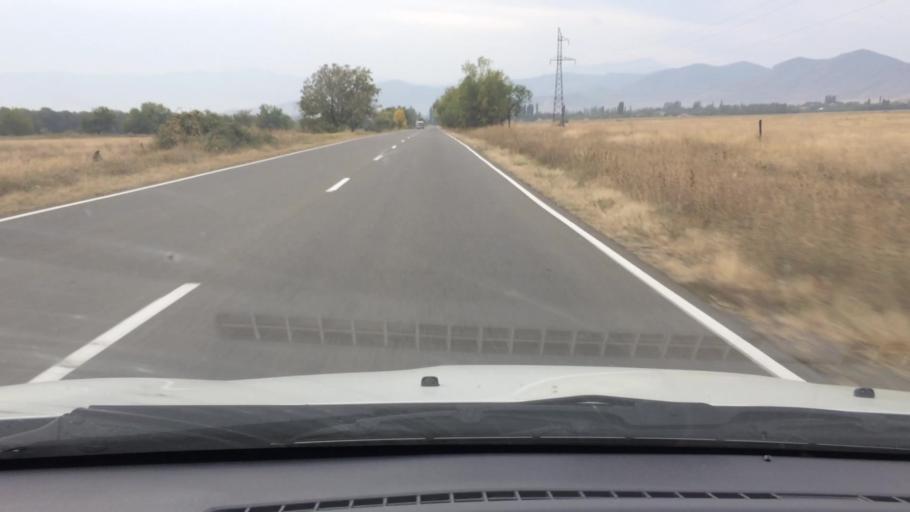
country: GE
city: Naghvarevi
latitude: 41.3379
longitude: 44.8098
